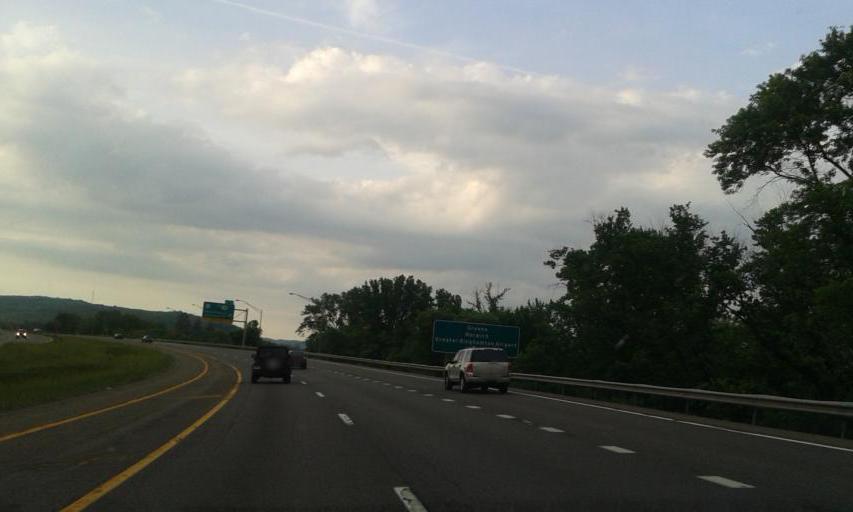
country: US
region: New York
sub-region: Broome County
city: Port Dickinson
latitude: 42.1485
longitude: -75.8971
